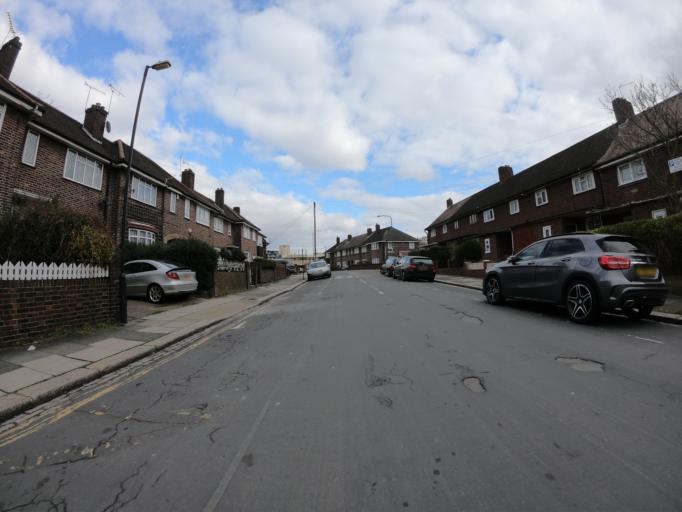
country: GB
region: England
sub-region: Greater London
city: Woolwich
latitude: 51.4920
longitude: 0.0595
